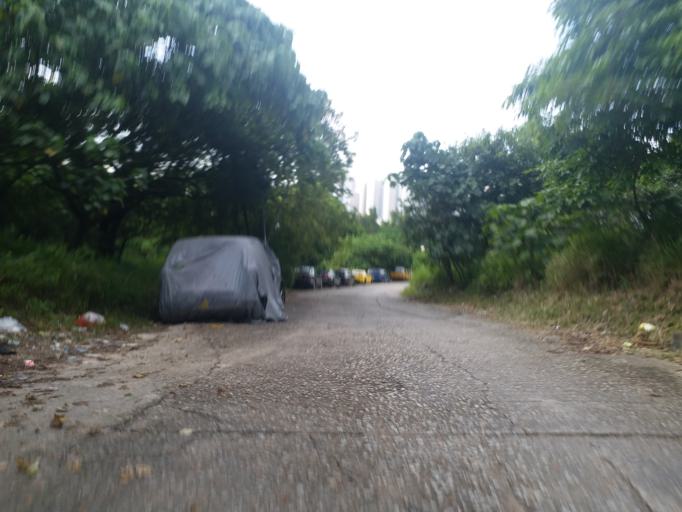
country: HK
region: Yuen Long
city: Yuen Long Kau Hui
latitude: 22.4381
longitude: 114.0011
